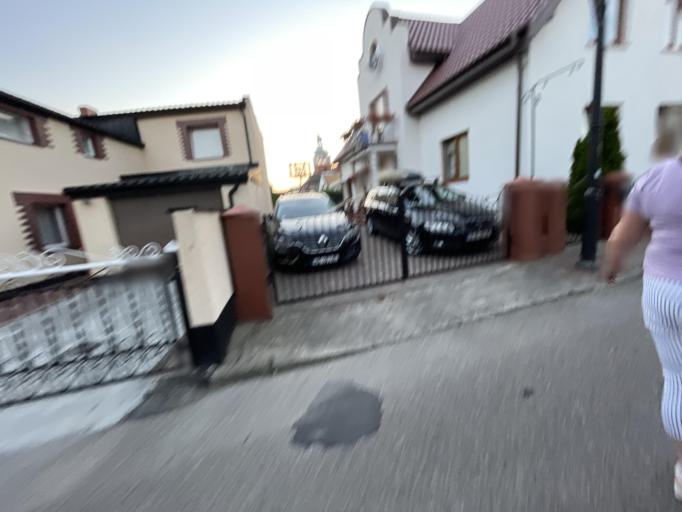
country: PL
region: Pomeranian Voivodeship
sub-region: Powiat pucki
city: Jastarnia
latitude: 54.7022
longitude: 18.6733
